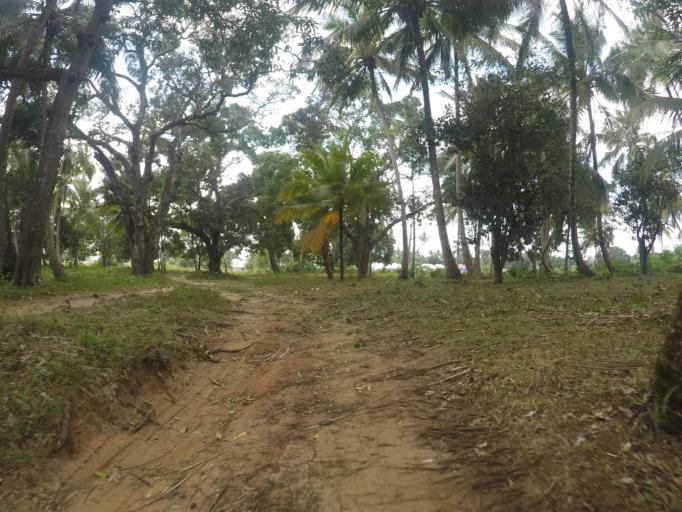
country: TZ
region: Zanzibar Urban/West
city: Zanzibar
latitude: -6.2055
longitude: 39.2388
